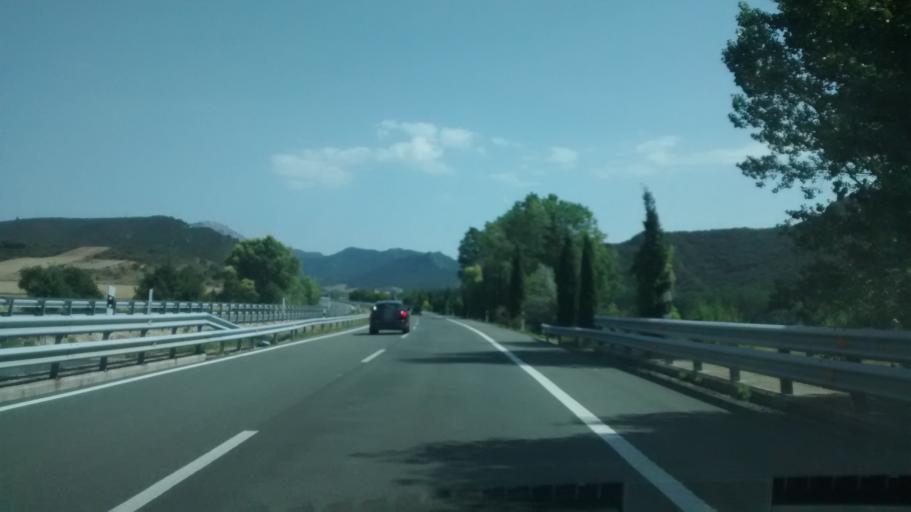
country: ES
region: Basque Country
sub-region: Provincia de Alava
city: Zambrana
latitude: 42.6444
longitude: -2.8747
